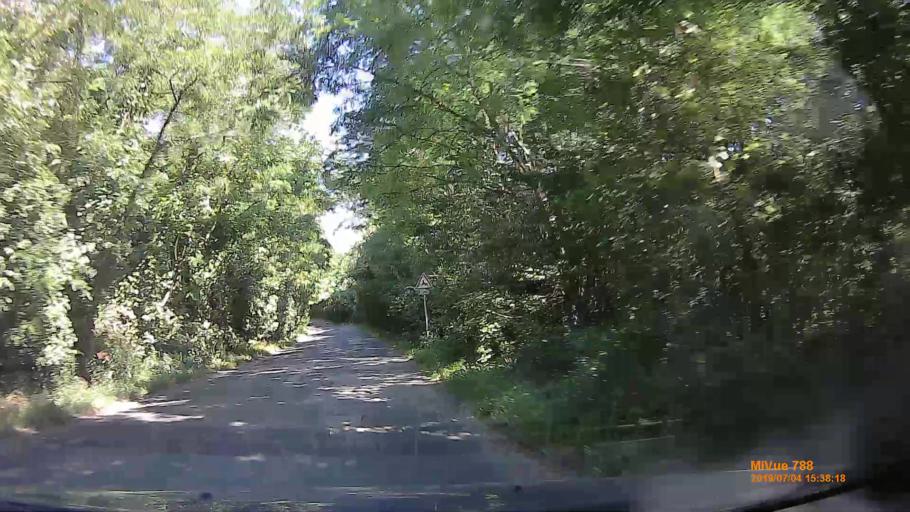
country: HU
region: Komarom-Esztergom
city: Tatabanya
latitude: 47.5548
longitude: 18.3938
